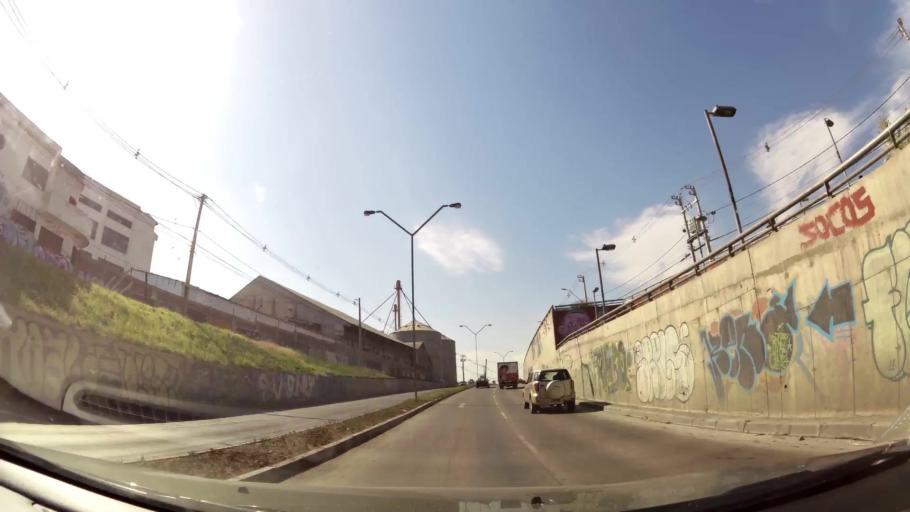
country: CL
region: Santiago Metropolitan
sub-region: Provincia de Maipo
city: San Bernardo
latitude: -33.5977
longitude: -70.6970
